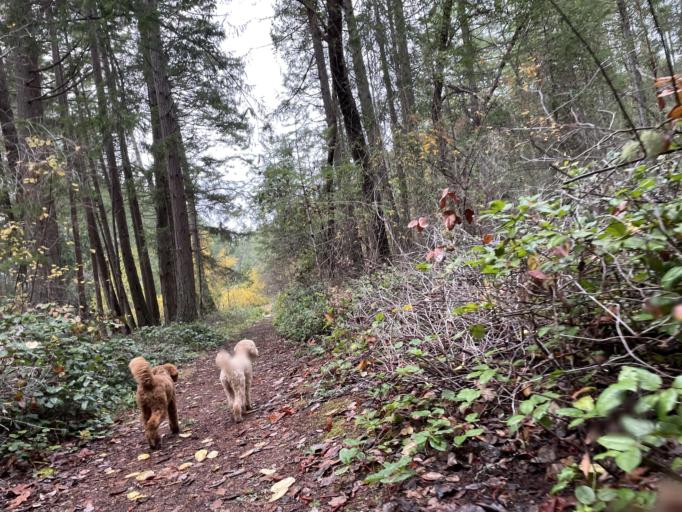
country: CA
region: British Columbia
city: North Cowichan
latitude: 48.9393
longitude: -123.5466
